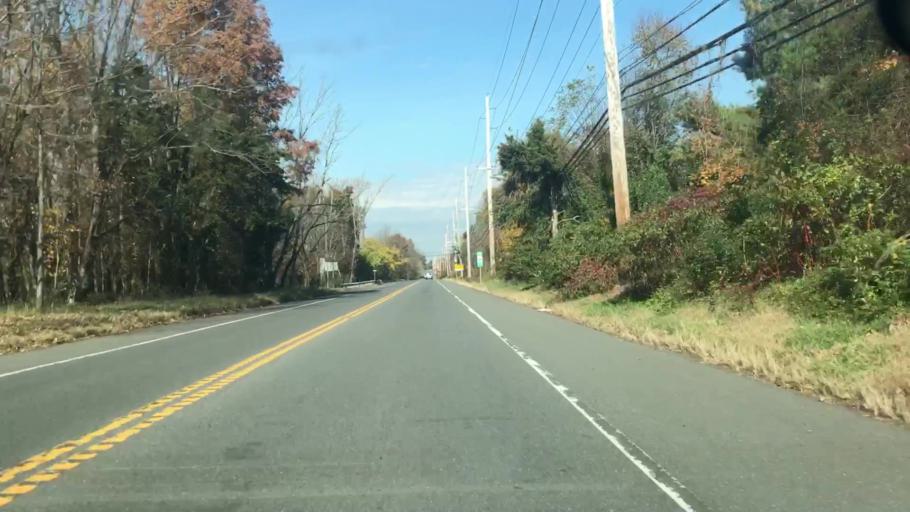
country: US
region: New Jersey
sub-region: Somerset County
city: Ten Mile Run
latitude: 40.4286
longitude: -74.6582
